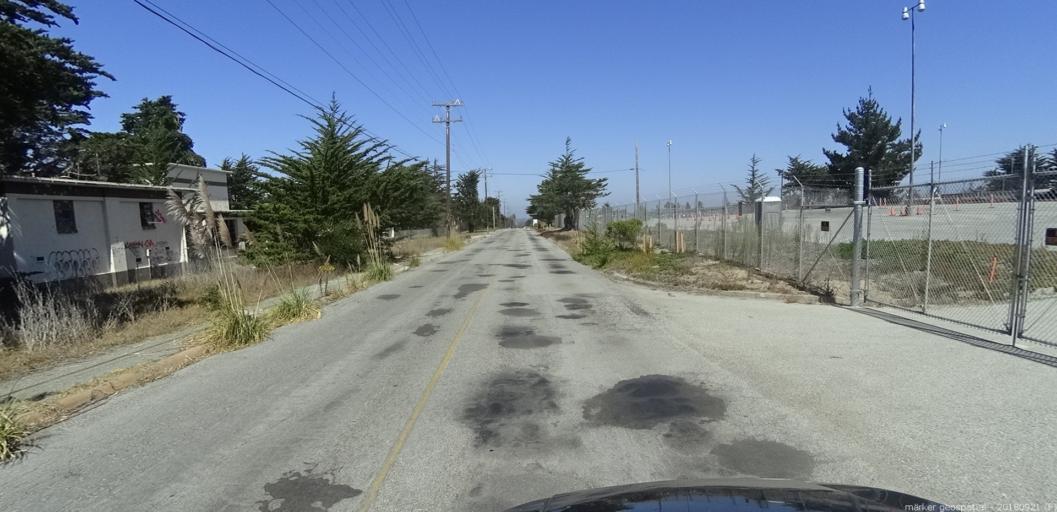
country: US
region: California
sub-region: Monterey County
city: Marina
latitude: 36.6450
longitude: -121.7898
